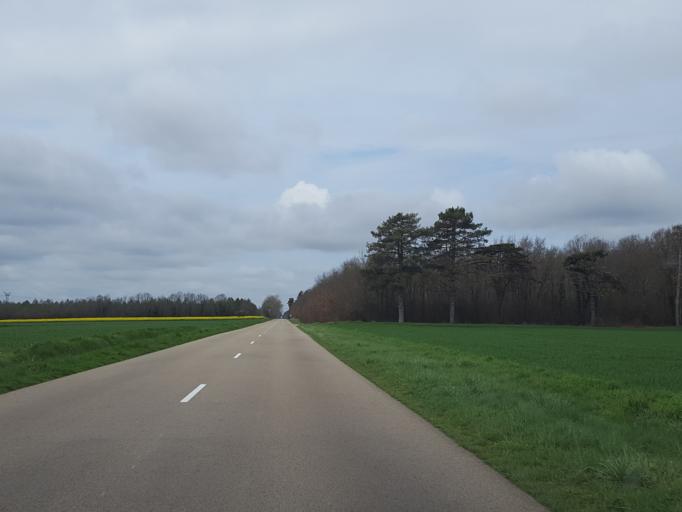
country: FR
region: Centre
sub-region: Departement du Loiret
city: Sainte-Genevieve-des-Bois
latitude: 47.8296
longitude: 2.7937
